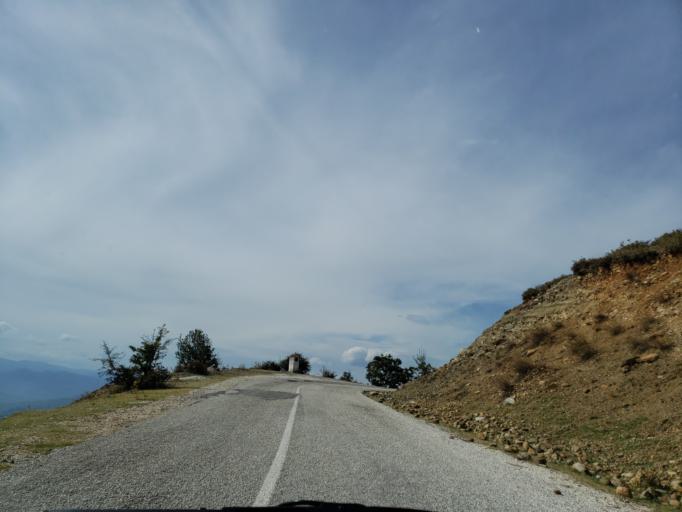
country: GR
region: Thessaly
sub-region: Trikala
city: Kastraki
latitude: 39.7521
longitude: 21.6609
